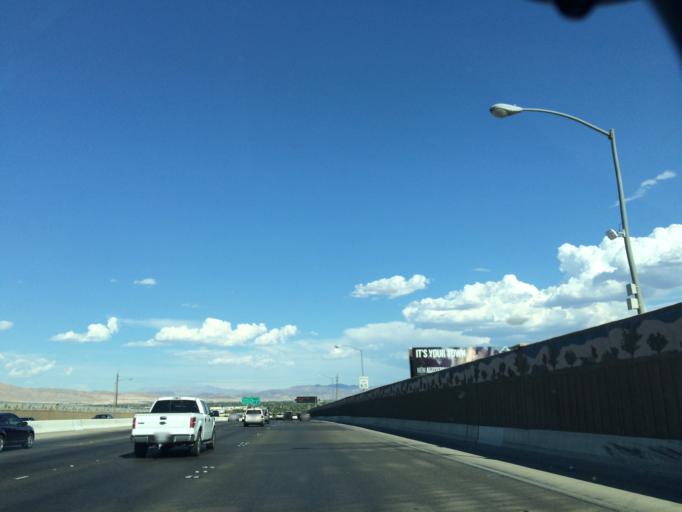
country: US
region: Nevada
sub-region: Clark County
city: Las Vegas
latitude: 36.1702
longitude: -115.1304
